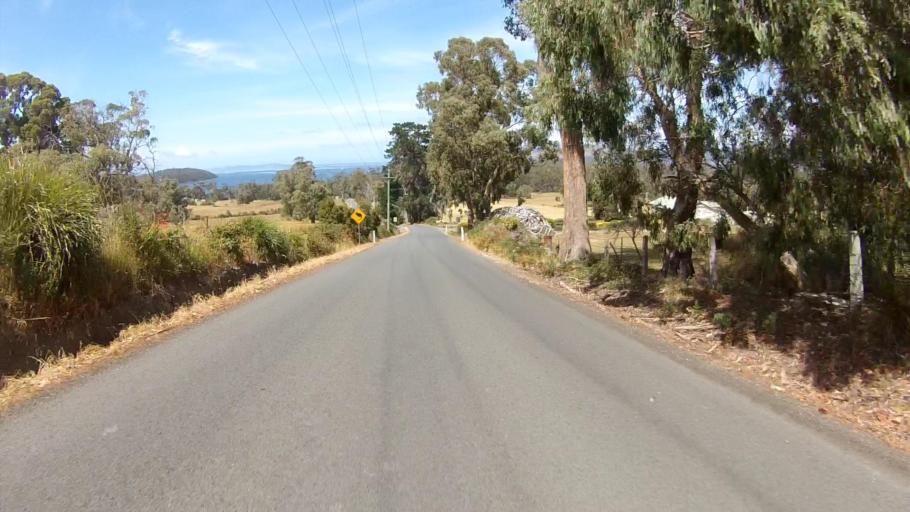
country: AU
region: Tasmania
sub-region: Huon Valley
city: Cygnet
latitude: -43.2339
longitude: 147.1261
